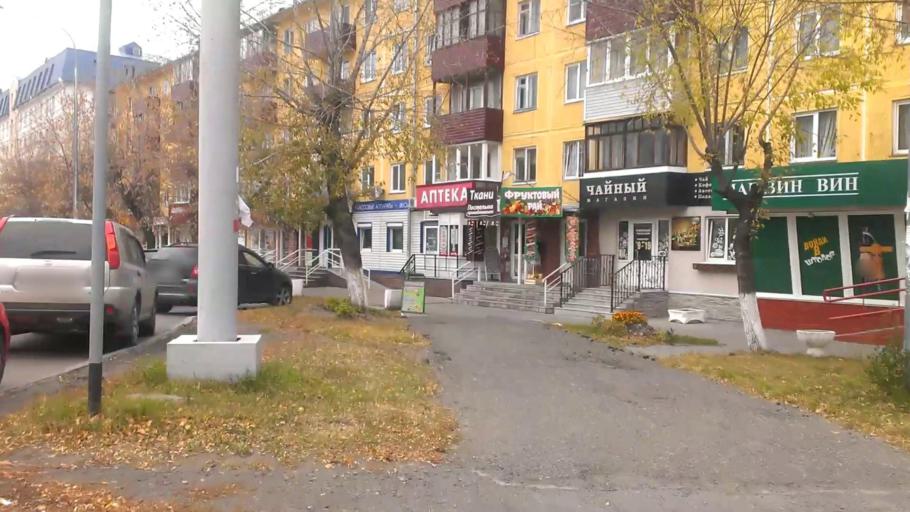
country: RU
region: Altai Krai
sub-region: Gorod Barnaulskiy
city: Barnaul
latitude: 53.3475
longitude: 83.7717
